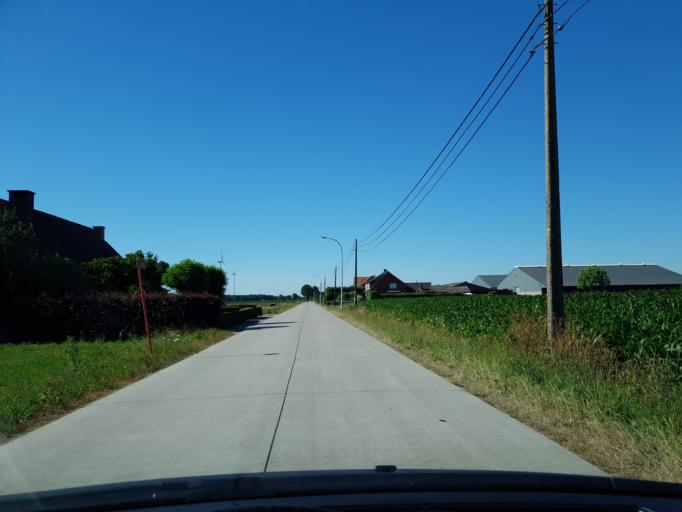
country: BE
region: Flanders
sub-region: Provincie Antwerpen
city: Hoogstraten
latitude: 51.4160
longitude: 4.7251
